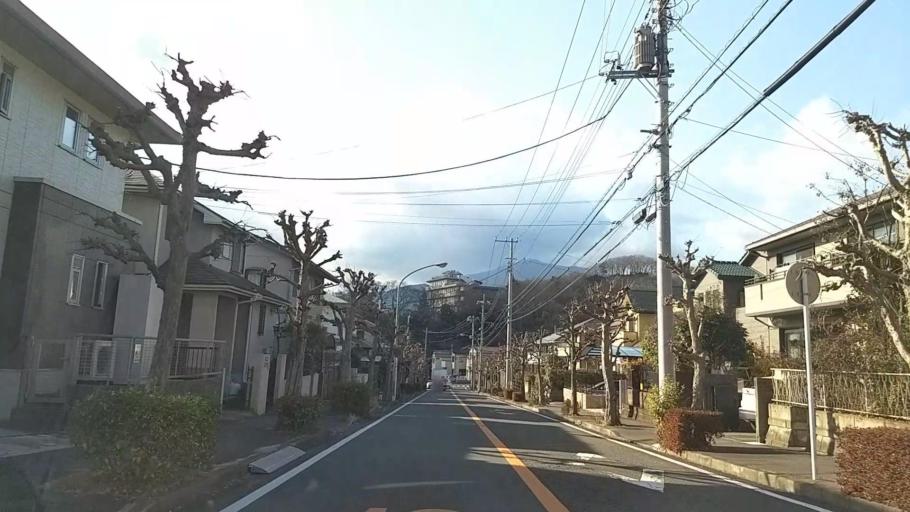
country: JP
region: Kanagawa
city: Atsugi
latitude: 35.4356
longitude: 139.3263
